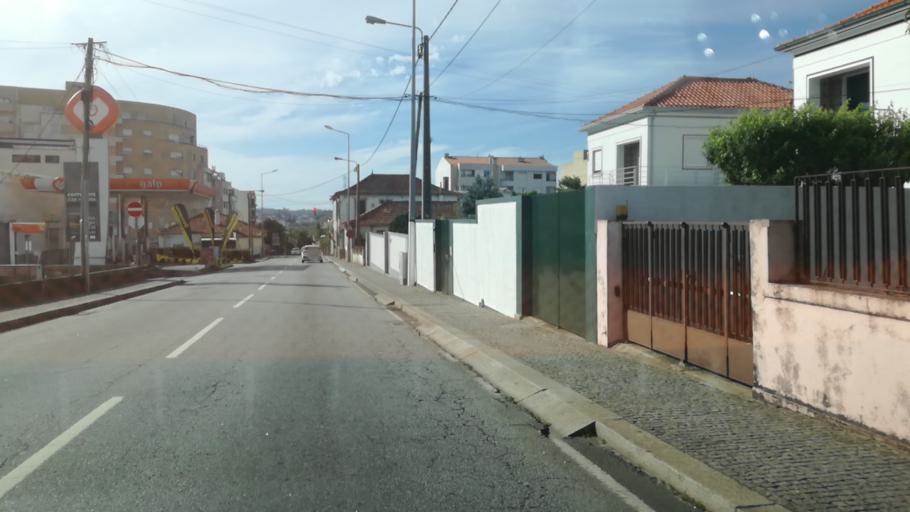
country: PT
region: Porto
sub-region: Maia
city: Nogueira
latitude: 41.2291
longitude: -8.5869
